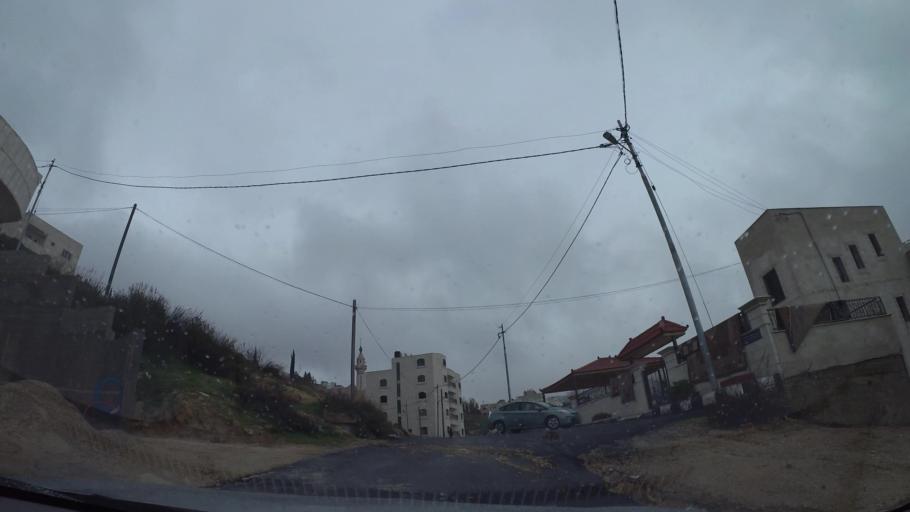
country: JO
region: Amman
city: Al Jubayhah
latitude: 32.0357
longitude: 35.8407
